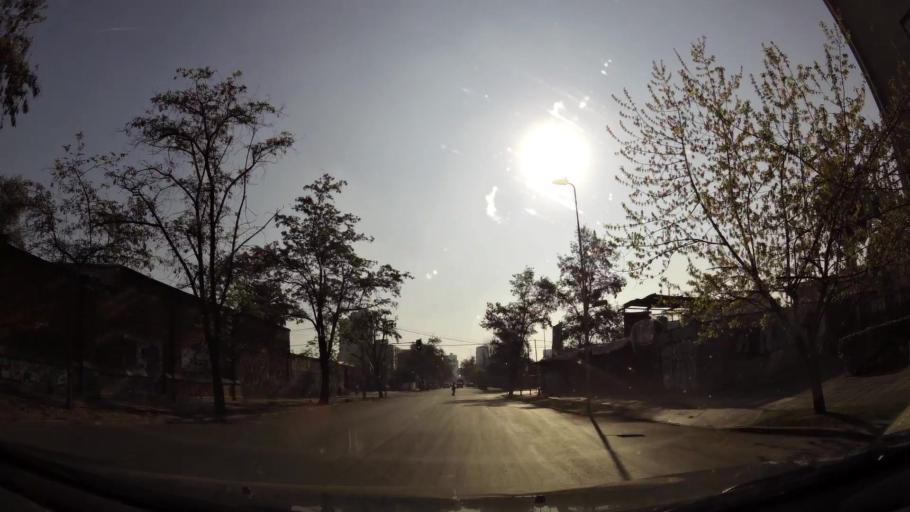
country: CL
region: Santiago Metropolitan
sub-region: Provincia de Santiago
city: Santiago
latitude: -33.4214
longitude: -70.6501
